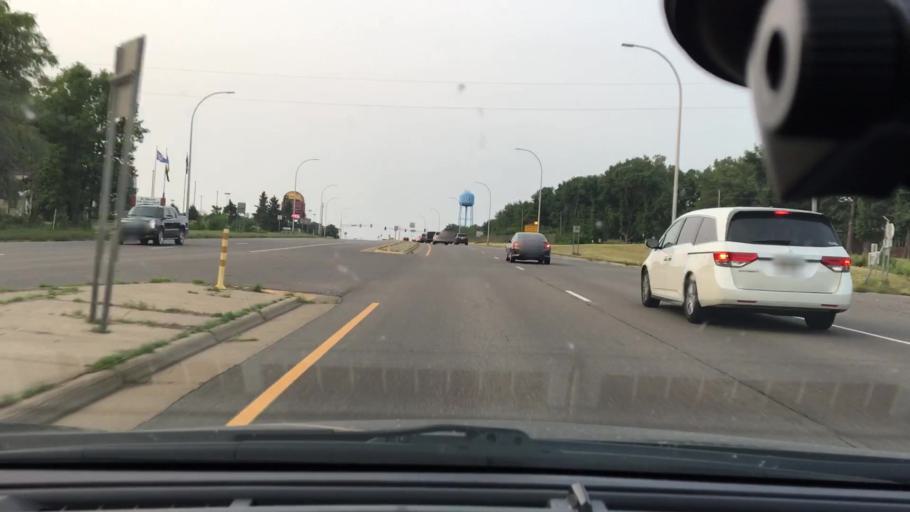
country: US
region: Minnesota
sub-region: Mille Lacs County
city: Vineland
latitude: 46.1770
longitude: -93.7567
